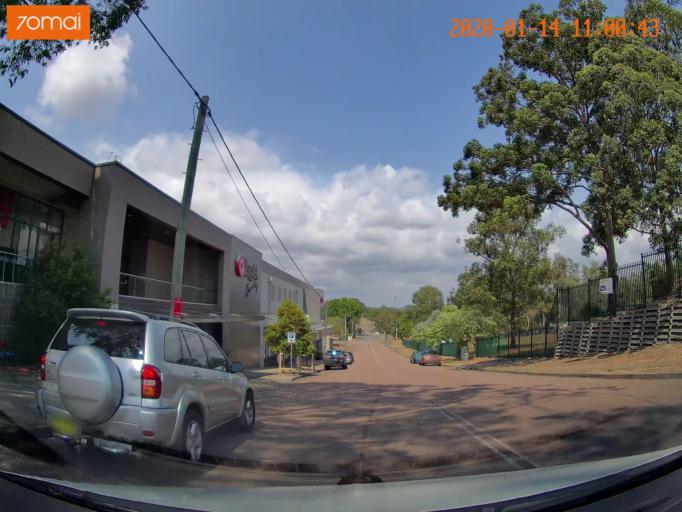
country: AU
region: New South Wales
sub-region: Lake Macquarie Shire
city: Dora Creek
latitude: -33.1061
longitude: 151.4880
